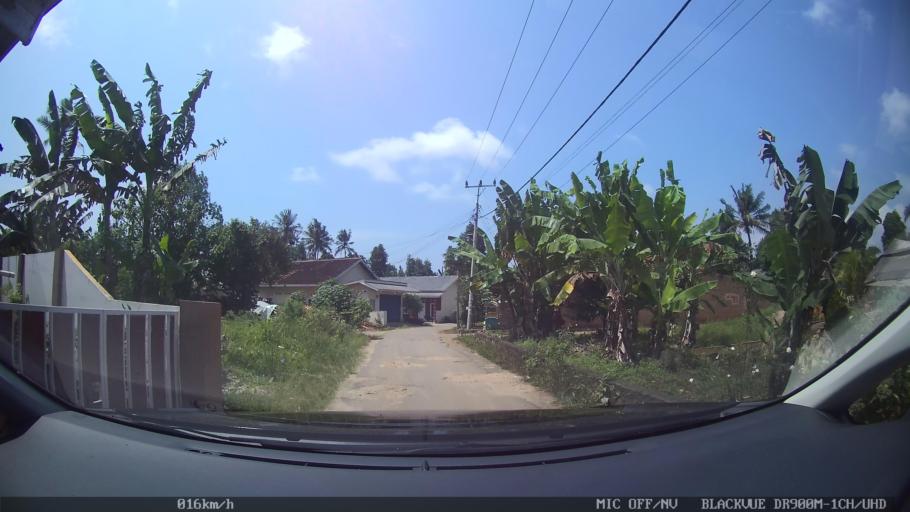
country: ID
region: Lampung
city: Kedaton
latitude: -5.3527
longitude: 105.2789
